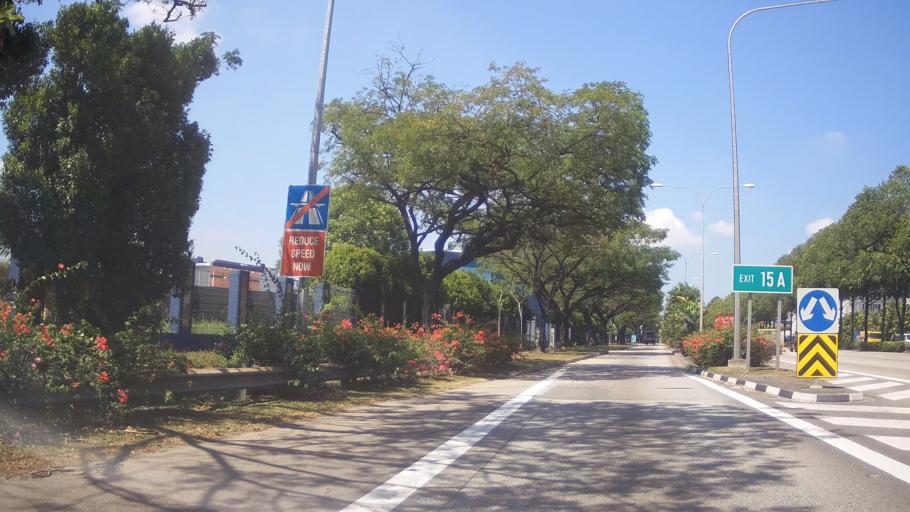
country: SG
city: Singapore
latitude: 1.3247
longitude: 103.7257
